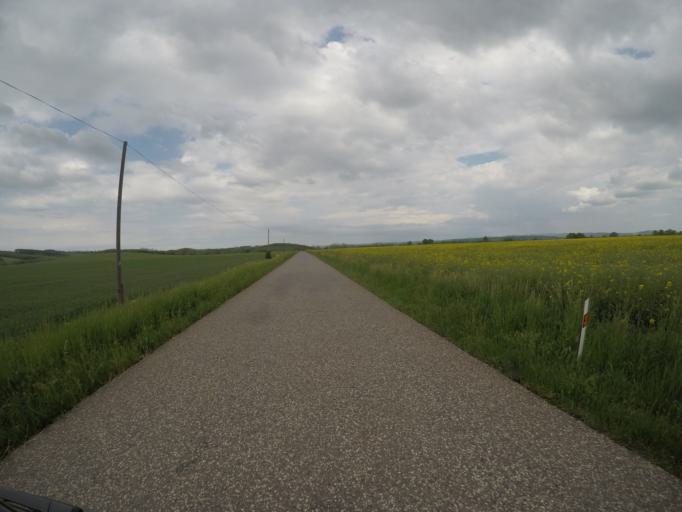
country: SK
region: Nitriansky
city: Sahy
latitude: 48.0706
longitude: 18.8599
